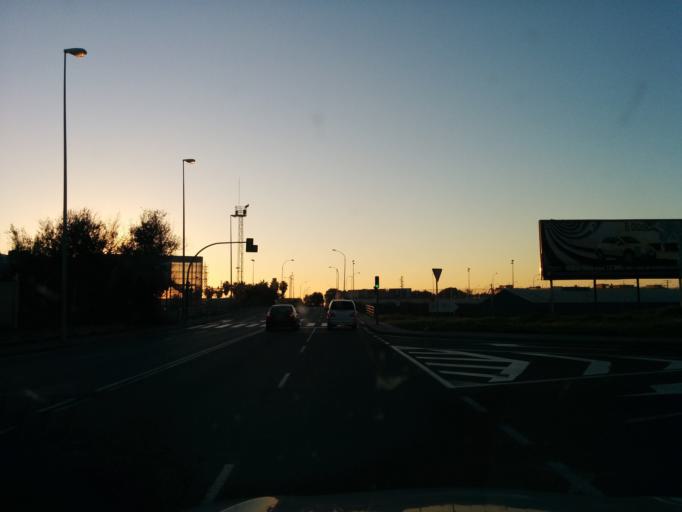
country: ES
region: Andalusia
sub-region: Provincia de Sevilla
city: Sevilla
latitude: 37.3796
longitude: -5.9365
